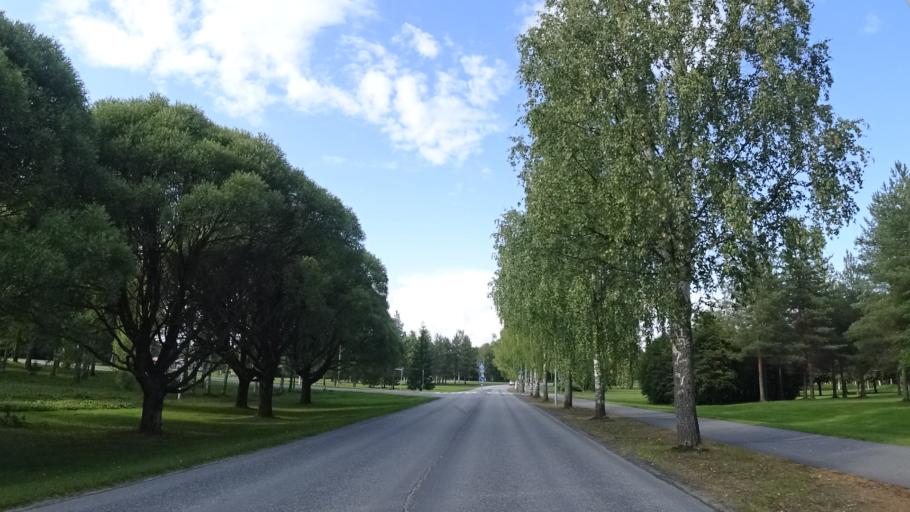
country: FI
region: North Karelia
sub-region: Pielisen Karjala
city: Lieksa
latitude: 63.3262
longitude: 30.0225
